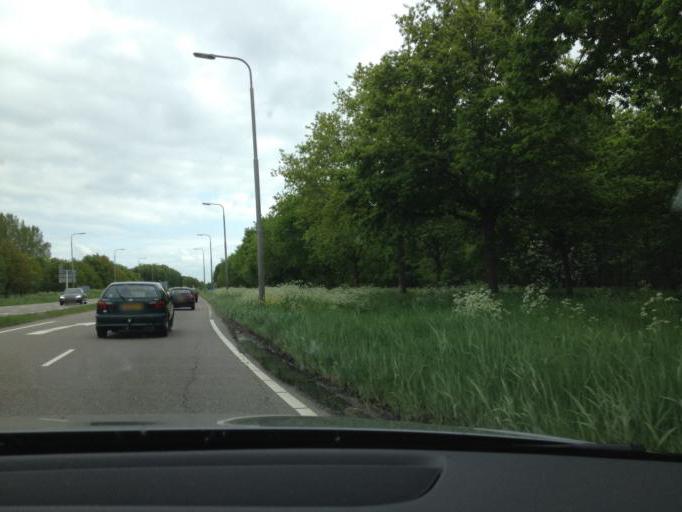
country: NL
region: Flevoland
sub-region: Gemeente Almere
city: Almere Stad
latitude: 52.3539
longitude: 5.2579
